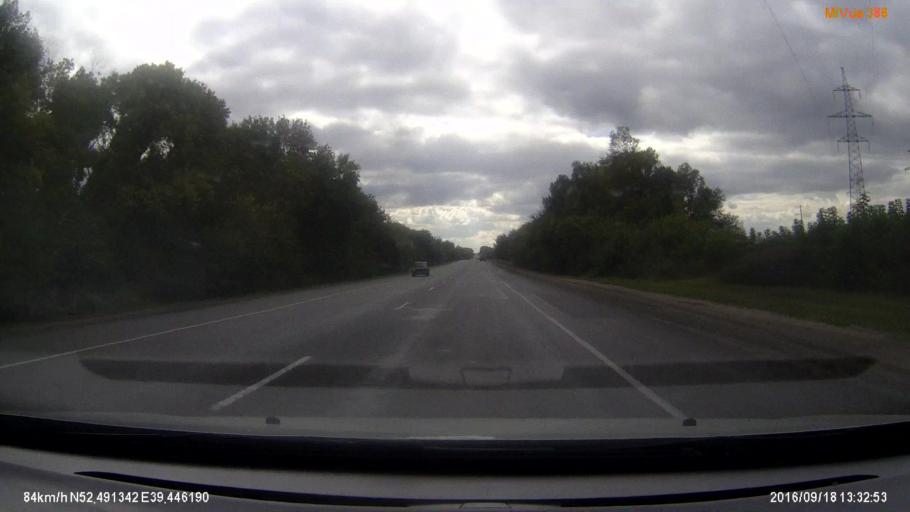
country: RU
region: Lipetsk
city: Borinskoye
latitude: 52.4586
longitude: 39.3842
